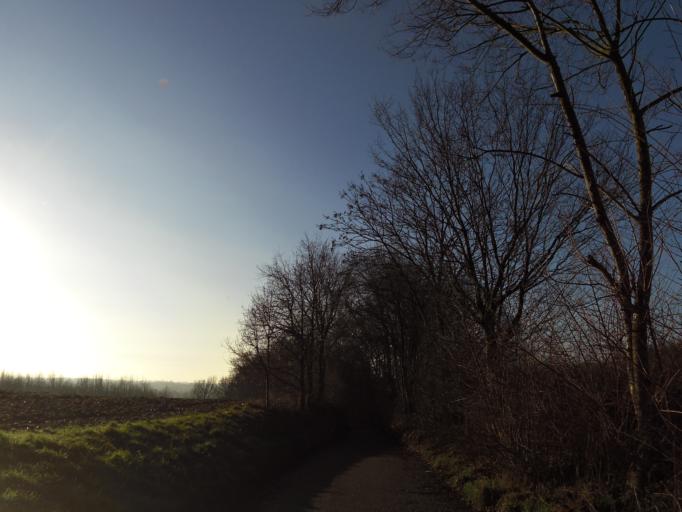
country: NL
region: Limburg
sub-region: Gemeente Kerkrade
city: Kerkrade
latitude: 50.9006
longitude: 6.0641
